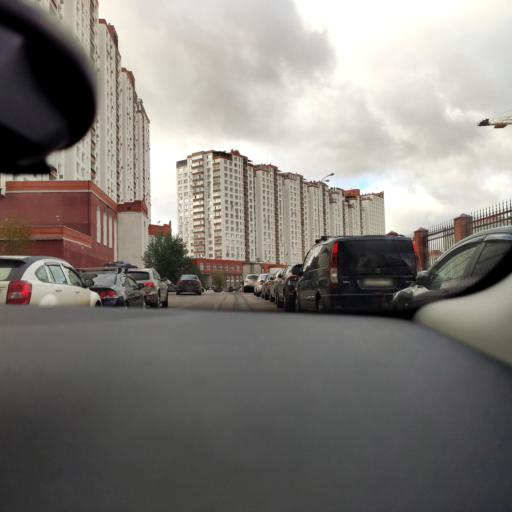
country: RU
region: Moskovskaya
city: Dzerzhinskiy
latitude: 55.6330
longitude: 37.8729
